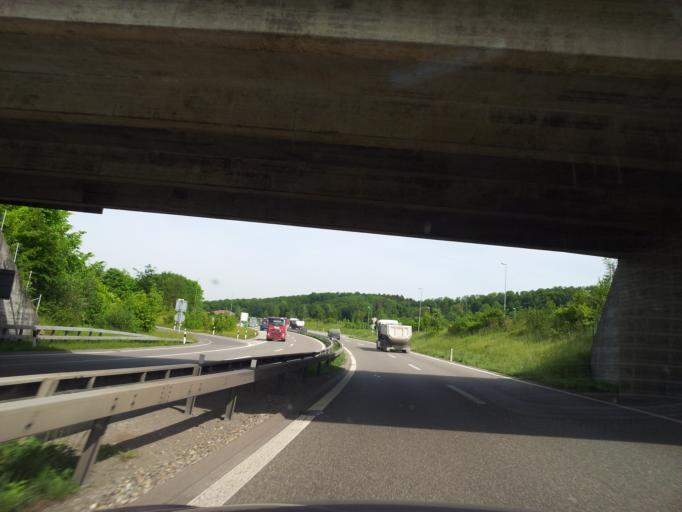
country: CH
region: Zurich
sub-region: Bezirk Buelach
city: Kloten / Freienberg (Chanzler-Chlini Chaseren)
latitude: 47.4613
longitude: 8.5754
